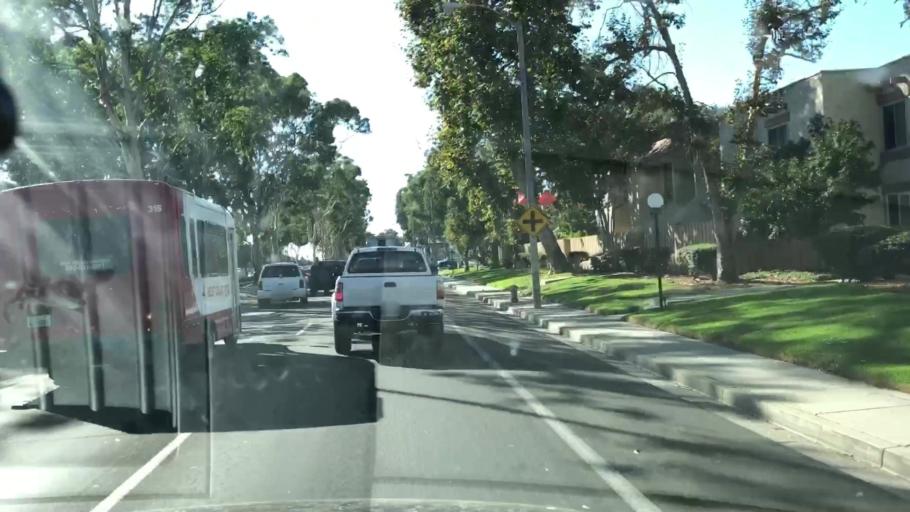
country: US
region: California
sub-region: Ventura County
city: Channel Islands Beach
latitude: 34.1760
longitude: -119.2051
